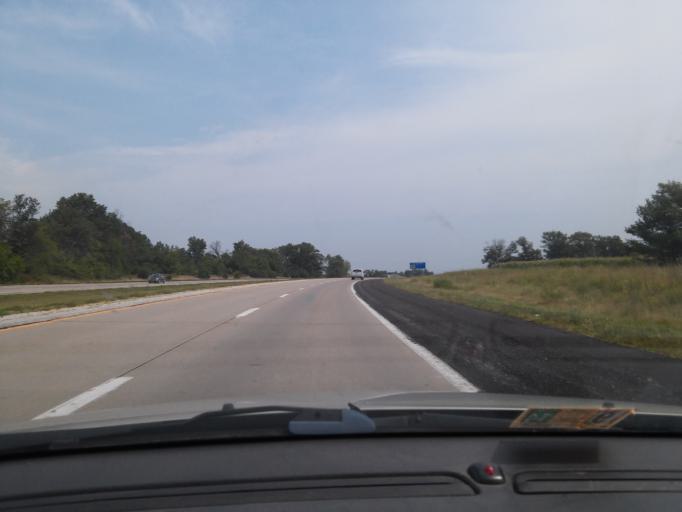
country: US
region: Missouri
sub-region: Audrain County
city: Mexico
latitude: 39.0080
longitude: -91.8927
